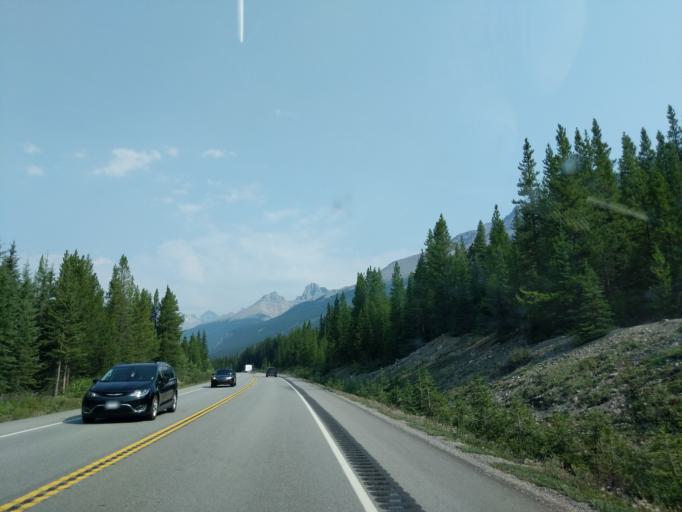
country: CA
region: Alberta
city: Lake Louise
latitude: 51.8027
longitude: -116.5801
